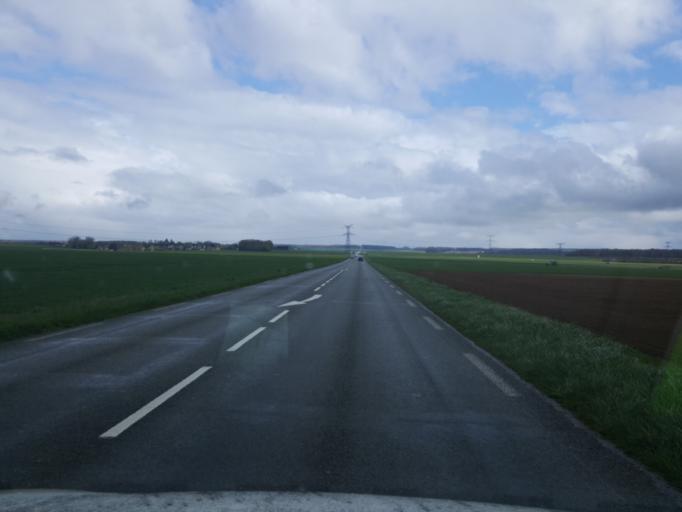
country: FR
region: Picardie
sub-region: Departement de l'Oise
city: Chaumont-en-Vexin
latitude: 49.3110
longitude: 1.8774
